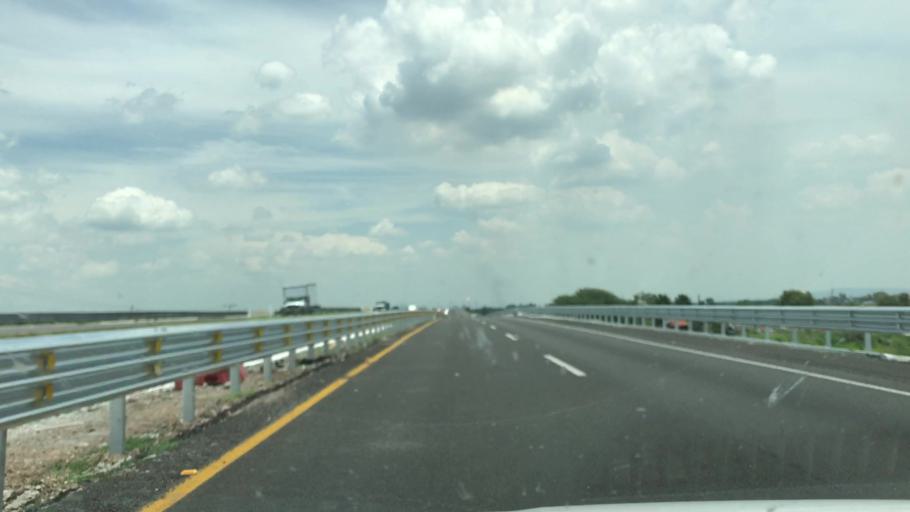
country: MX
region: Guanajuato
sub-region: Salamanca
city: San Vicente de Flores
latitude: 20.6130
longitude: -101.2227
